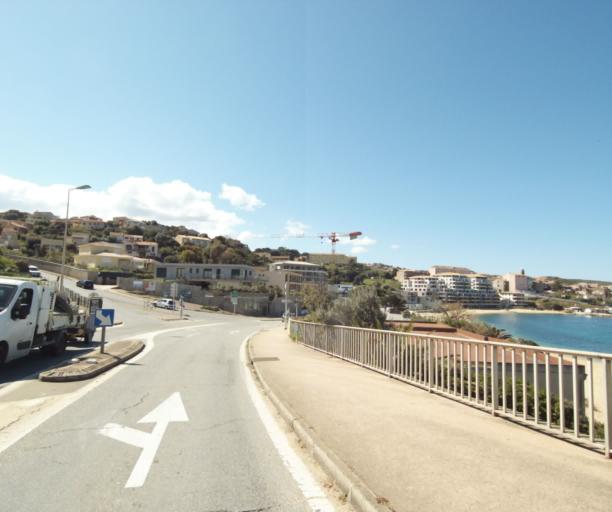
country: FR
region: Corsica
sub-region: Departement de la Corse-du-Sud
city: Propriano
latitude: 41.6789
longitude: 8.9110
